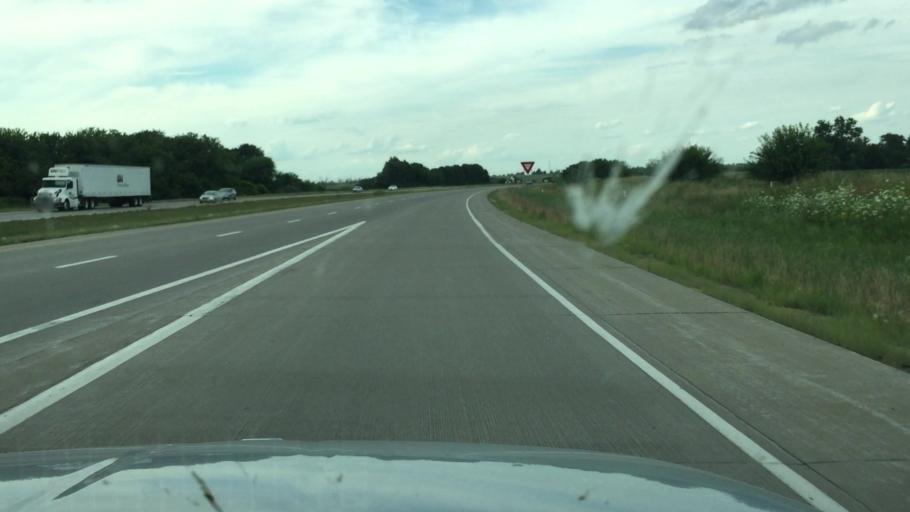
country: US
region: Iowa
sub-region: Scott County
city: Blue Grass
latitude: 41.5420
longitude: -90.6775
